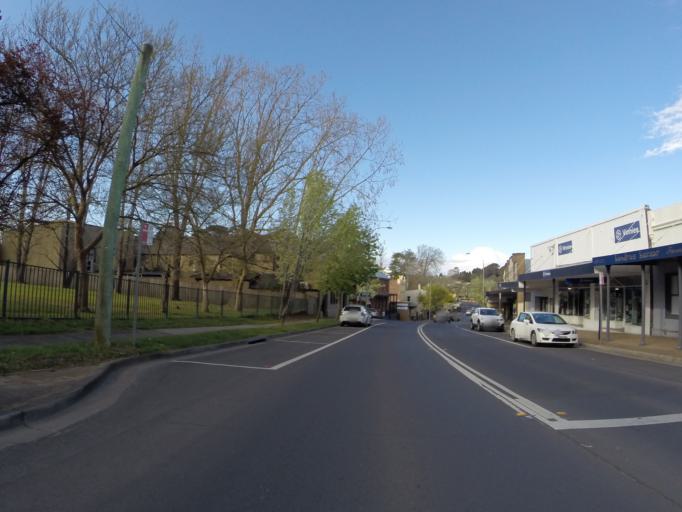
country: AU
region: New South Wales
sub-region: Wingecarribee
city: Moss Vale
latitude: -34.5516
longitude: 150.3673
